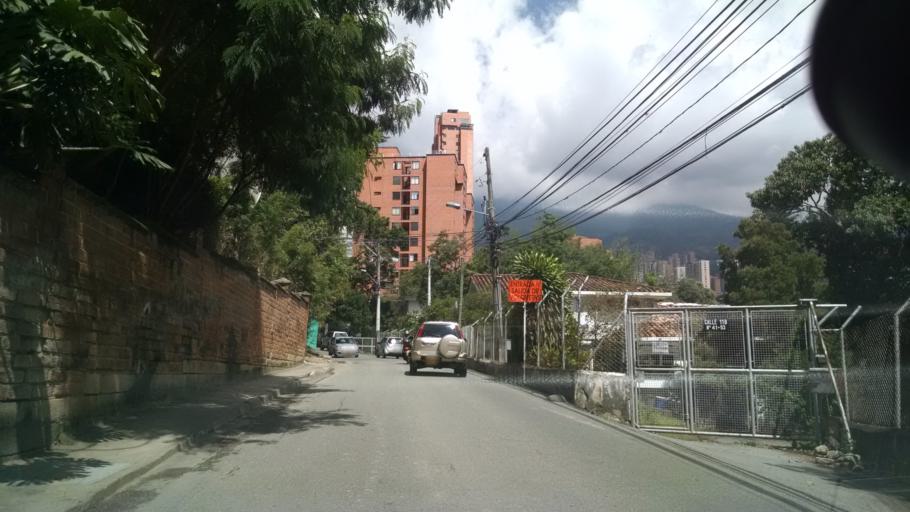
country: CO
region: Antioquia
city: Medellin
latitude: 6.2120
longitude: -75.5688
